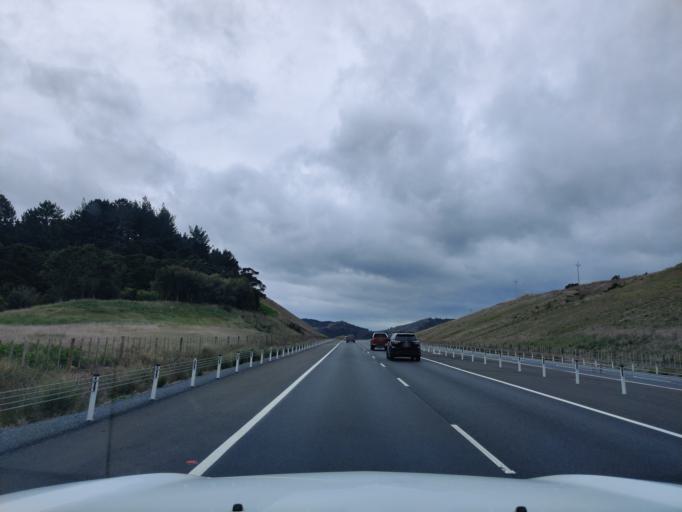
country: NZ
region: Waikato
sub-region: Waikato District
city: Ngaruawahia
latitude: -37.5441
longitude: 175.1903
